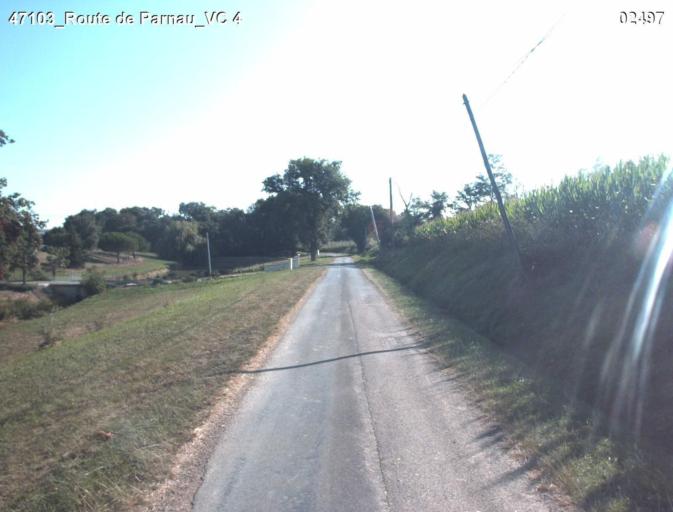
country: FR
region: Aquitaine
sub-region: Departement du Lot-et-Garonne
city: Nerac
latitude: 44.0802
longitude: 0.3581
